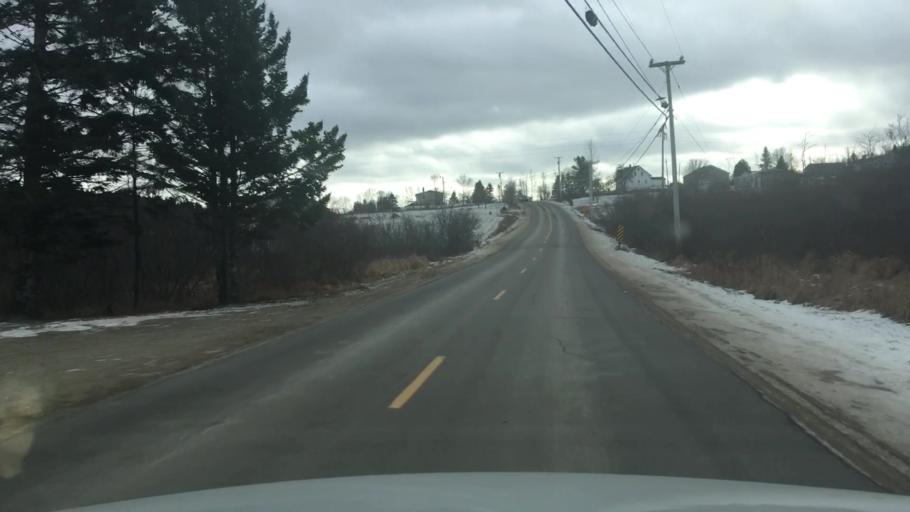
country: US
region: Maine
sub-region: Washington County
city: Machias
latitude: 44.6778
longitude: -67.4674
